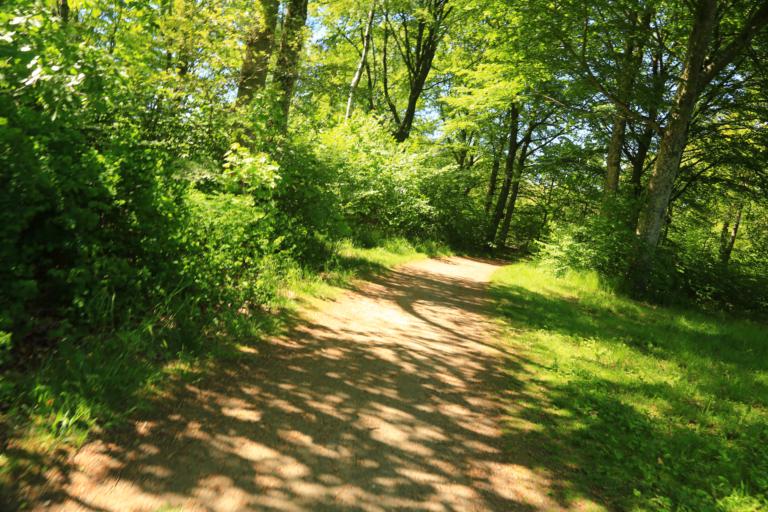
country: SE
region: Halland
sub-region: Varbergs Kommun
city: Varberg
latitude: 57.0993
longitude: 12.2674
